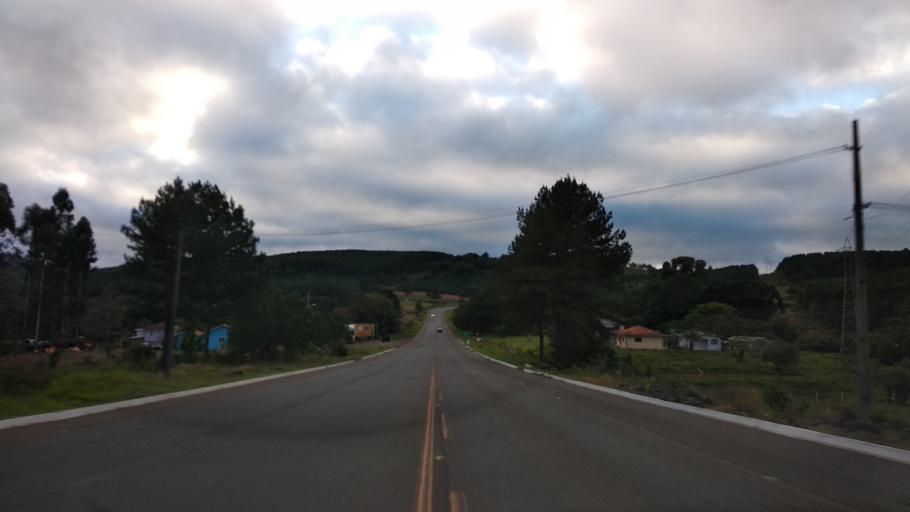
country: BR
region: Santa Catarina
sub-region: Campos Novos
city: Campos Novos
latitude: -27.4956
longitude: -50.9579
